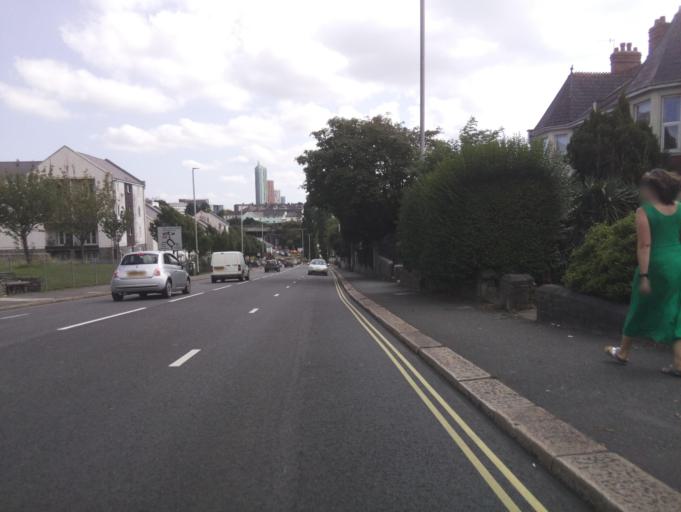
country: GB
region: England
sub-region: Plymouth
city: Plymouth
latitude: 50.3789
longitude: -4.1497
